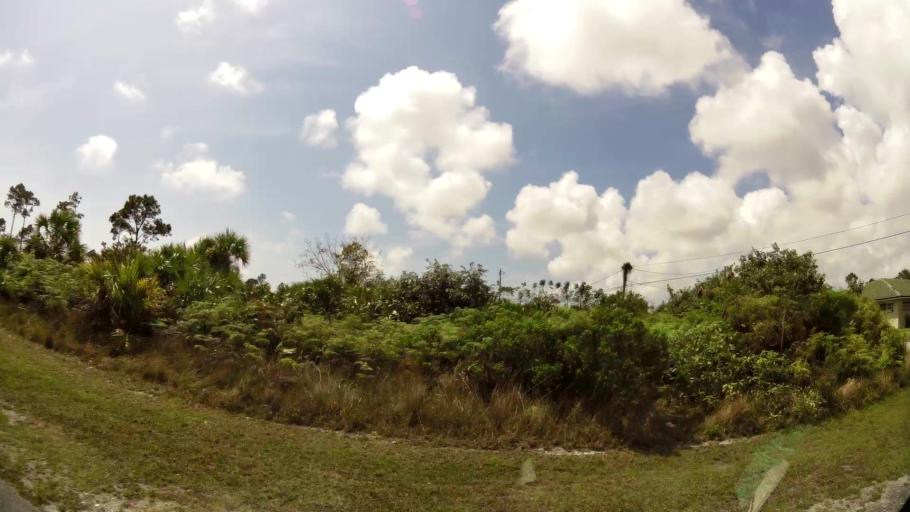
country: BS
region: Freeport
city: Freeport
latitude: 26.5159
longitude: -78.7225
